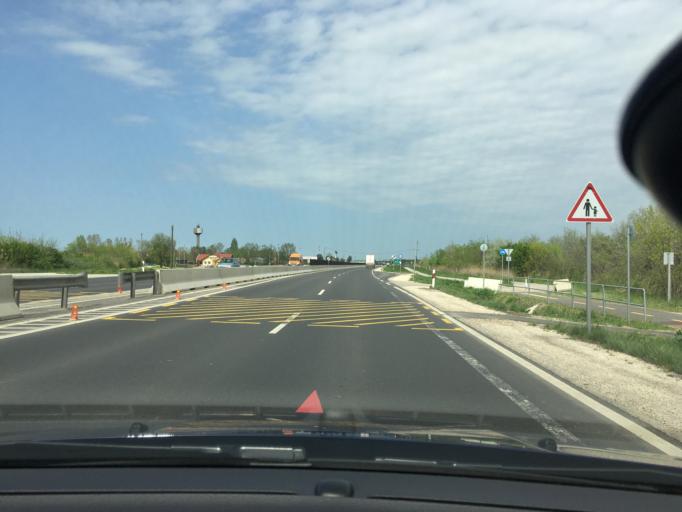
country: HU
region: Csongrad
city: Algyo
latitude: 46.3086
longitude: 20.1843
